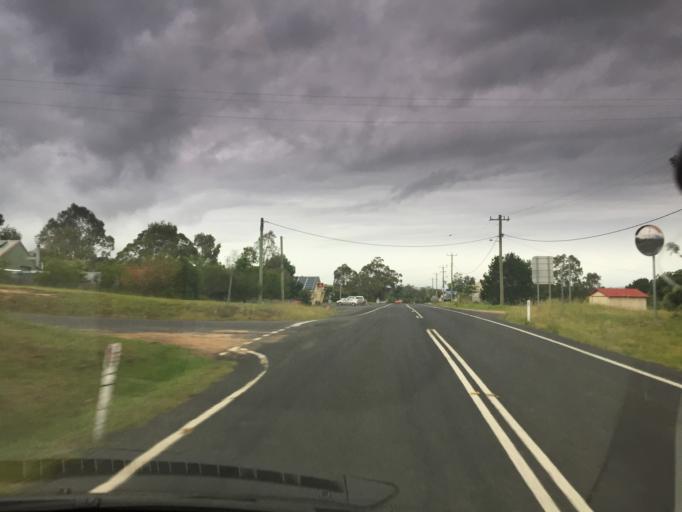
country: AU
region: New South Wales
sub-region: Bega Valley
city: Bega
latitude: -36.6249
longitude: 149.5644
